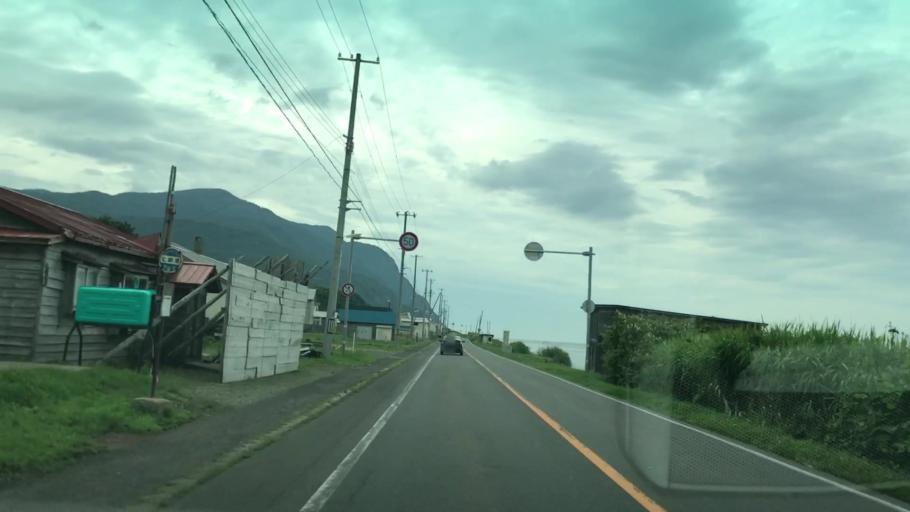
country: JP
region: Hokkaido
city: Iwanai
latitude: 42.9714
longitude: 140.4813
